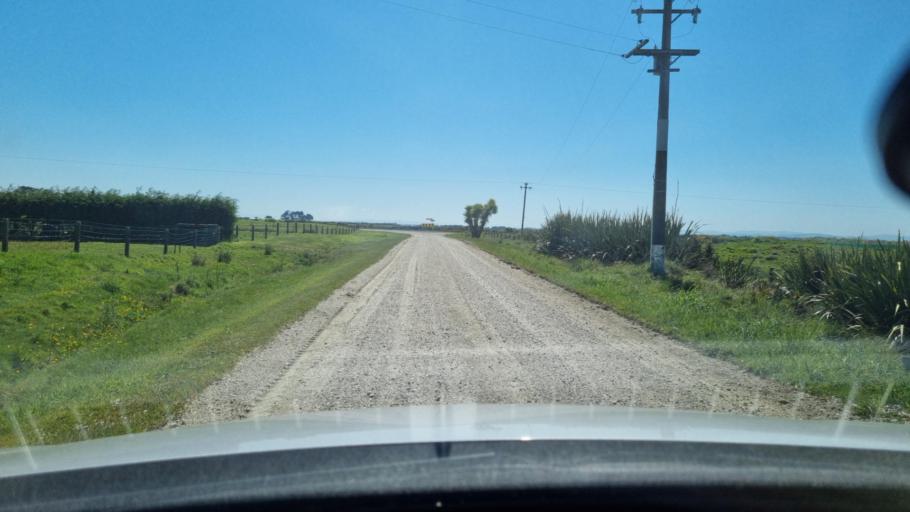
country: NZ
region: Southland
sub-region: Invercargill City
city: Invercargill
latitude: -46.4104
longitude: 168.2634
